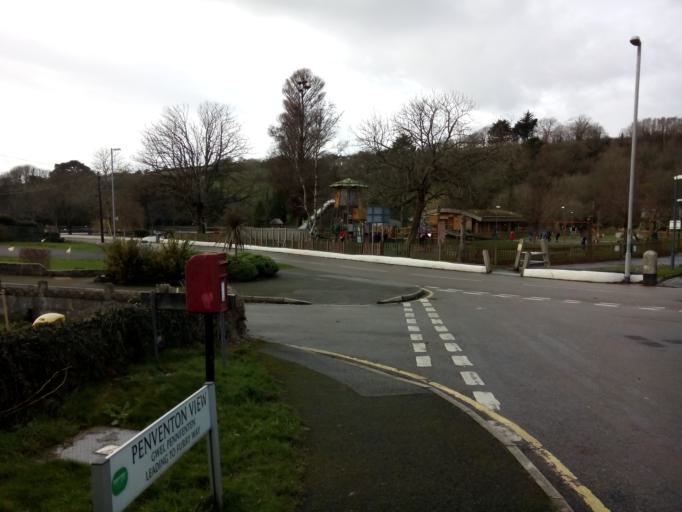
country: GB
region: England
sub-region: Cornwall
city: Helston
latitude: 50.0986
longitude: -5.2786
